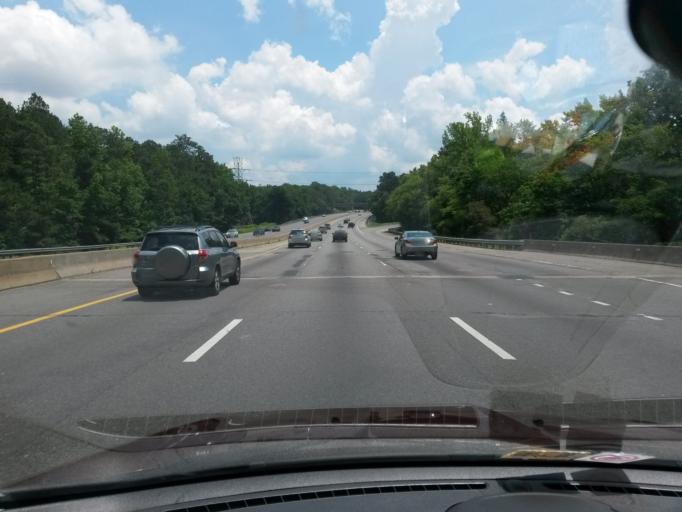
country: US
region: Virginia
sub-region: Chesterfield County
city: Chester
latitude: 37.3811
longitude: -77.4129
